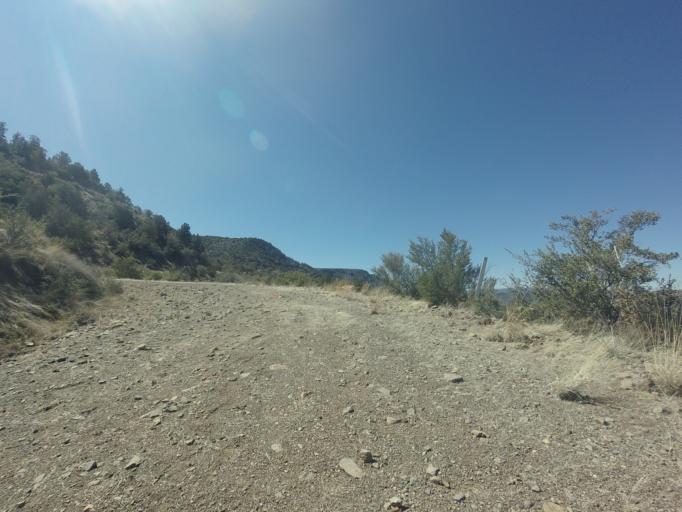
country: US
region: Arizona
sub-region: Gila County
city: Pine
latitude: 34.4021
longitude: -111.6099
